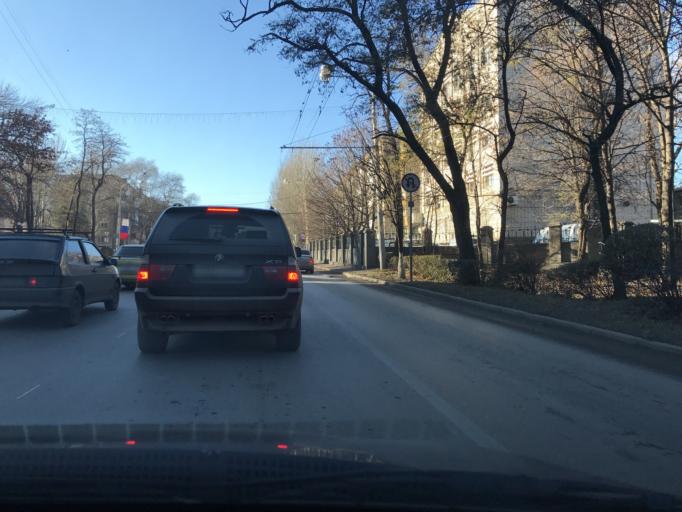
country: RU
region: Rostov
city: Rostov-na-Donu
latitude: 47.2111
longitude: 39.6766
